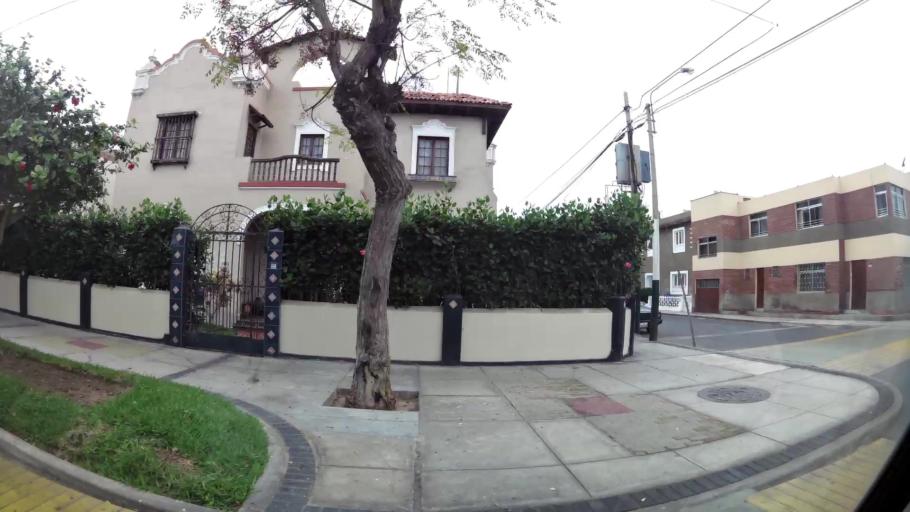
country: PE
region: Callao
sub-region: Callao
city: Callao
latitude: -12.0711
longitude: -77.1616
